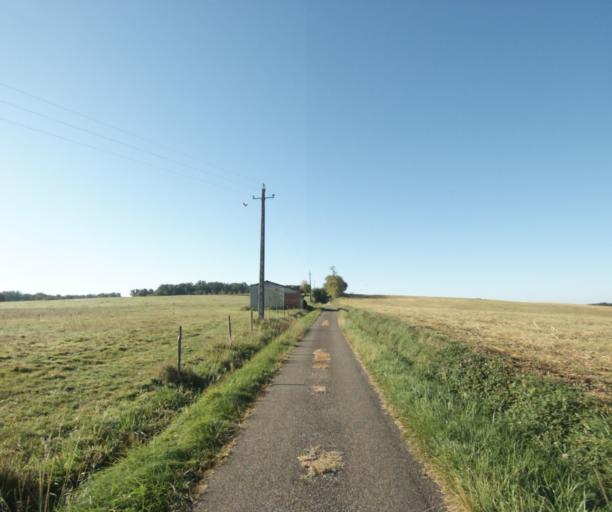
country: FR
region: Midi-Pyrenees
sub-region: Departement du Gers
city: Gondrin
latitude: 43.8459
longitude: 0.2245
